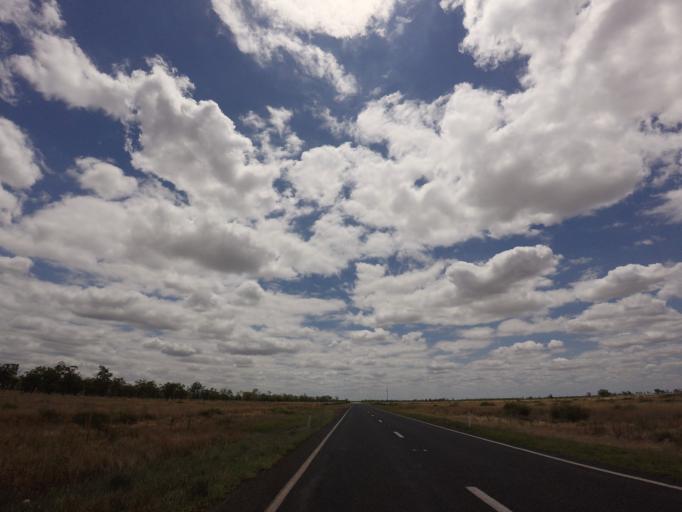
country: AU
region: New South Wales
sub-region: Moree Plains
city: Boggabilla
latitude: -28.6760
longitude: 150.3103
